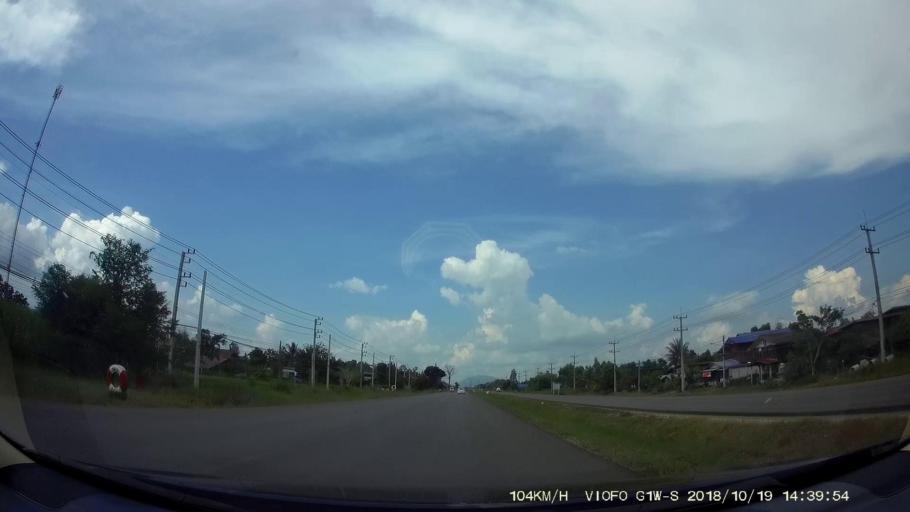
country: TH
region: Chaiyaphum
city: Kaeng Khro
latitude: 16.2326
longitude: 102.1950
